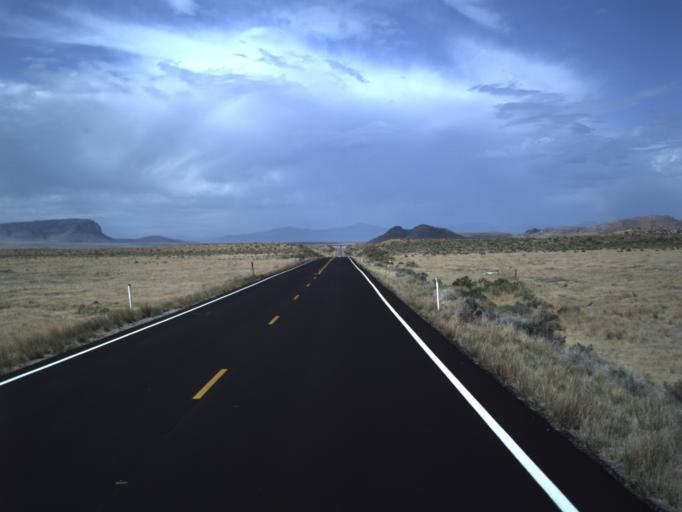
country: US
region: Utah
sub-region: Tooele County
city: Wendover
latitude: 41.4110
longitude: -113.9280
